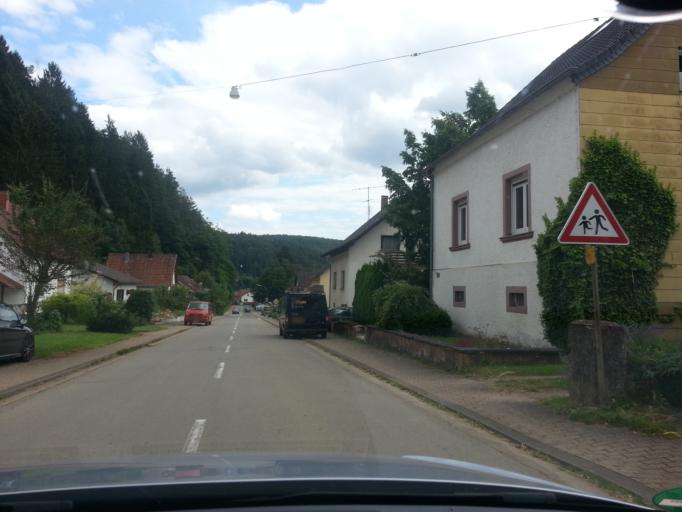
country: DE
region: Saarland
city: Beckingen
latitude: 49.4320
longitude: 6.7263
